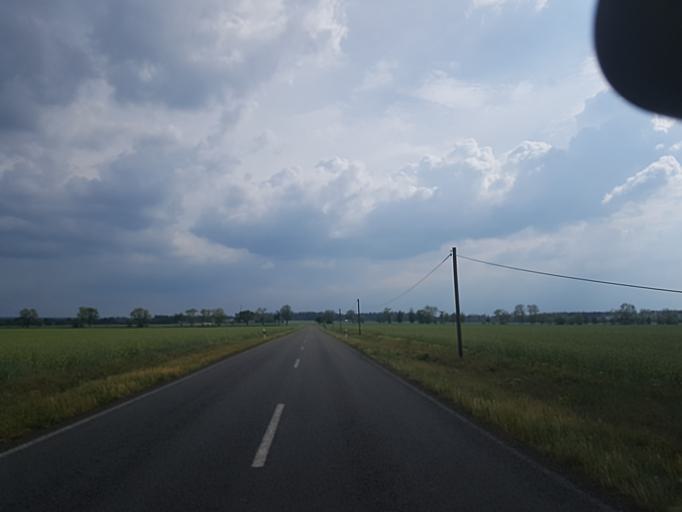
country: DE
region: Saxony-Anhalt
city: Rodleben
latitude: 51.9980
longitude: 12.2321
